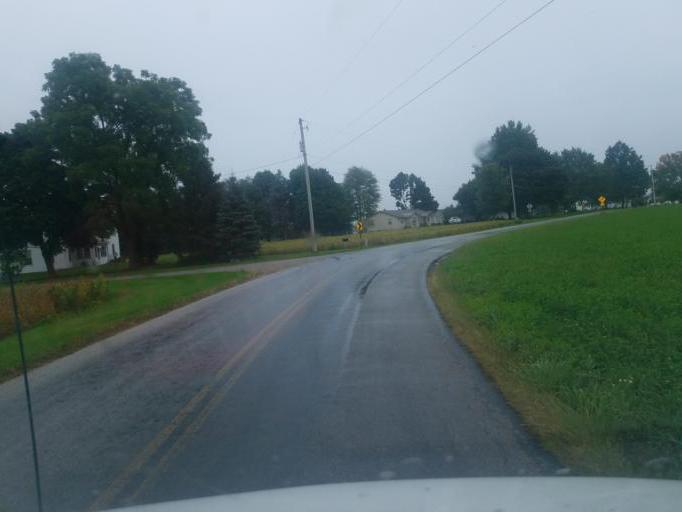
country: US
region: Ohio
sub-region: Medina County
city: Seville
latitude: 40.9823
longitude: -81.8307
